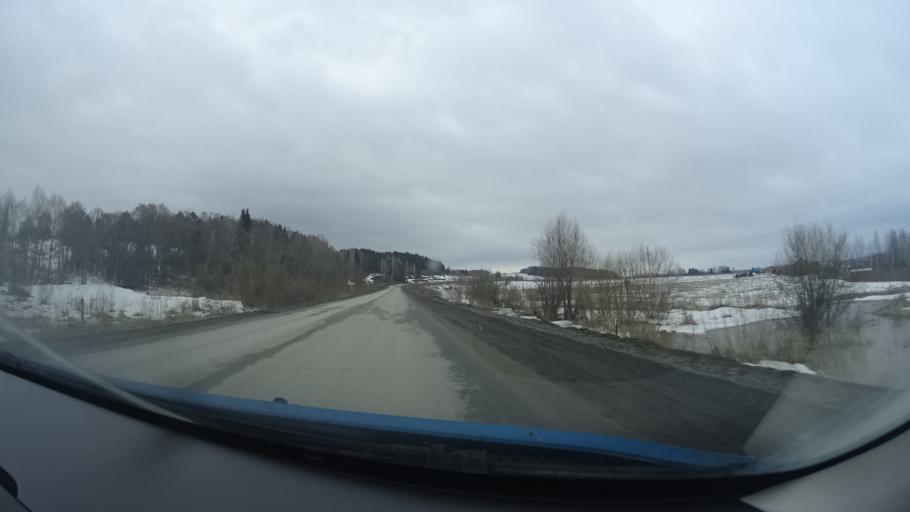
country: RU
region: Perm
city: Osa
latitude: 57.2218
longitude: 55.5889
